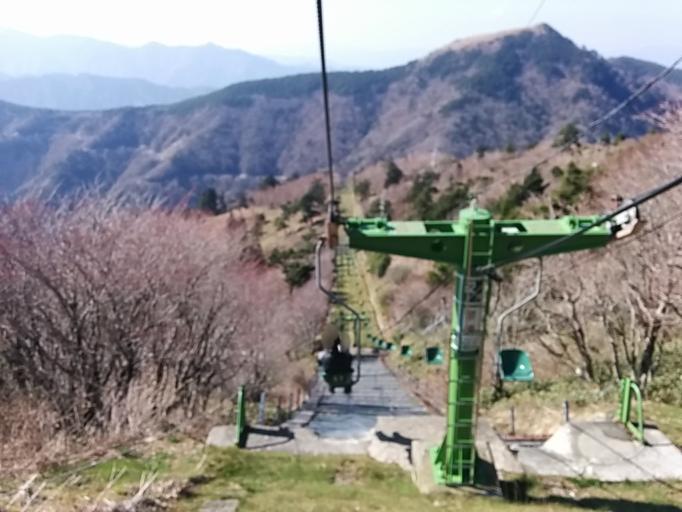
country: JP
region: Tokushima
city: Wakimachi
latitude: 33.8607
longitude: 134.0922
